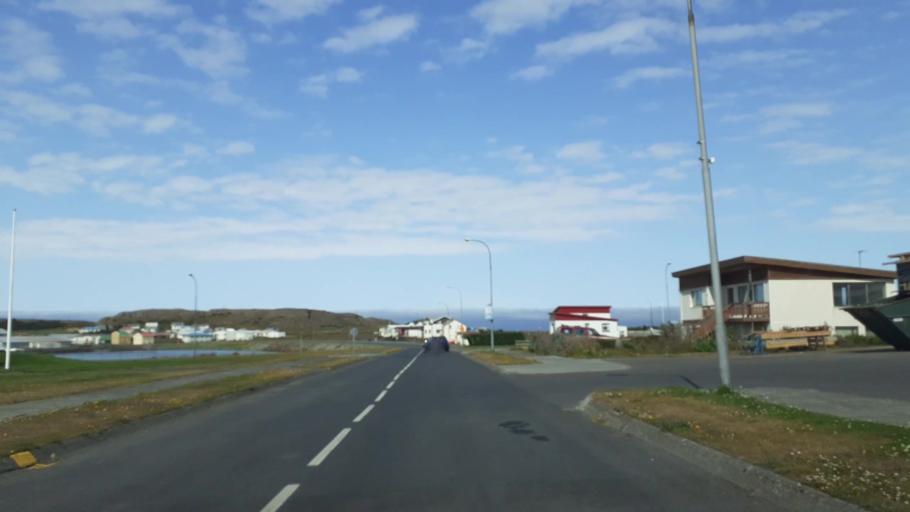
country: IS
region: Northwest
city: Saudarkrokur
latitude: 65.8243
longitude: -20.3063
